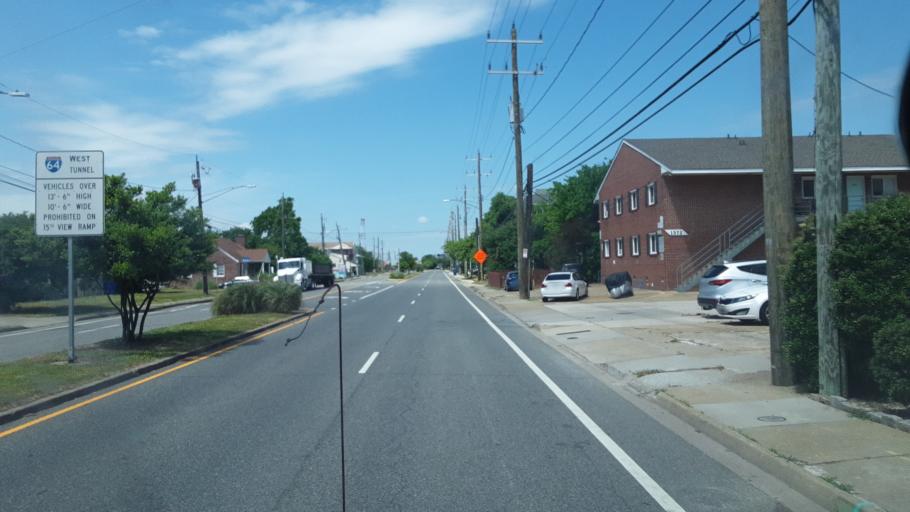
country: US
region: Virginia
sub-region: City of Hampton
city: East Hampton
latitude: 36.9672
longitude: -76.2884
